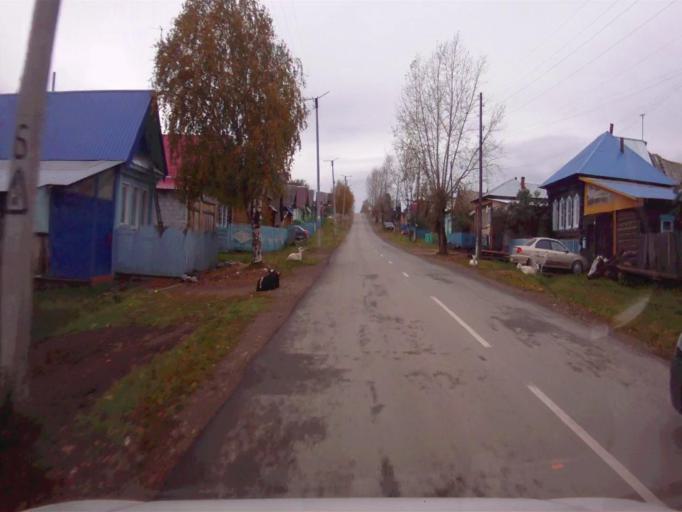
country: RU
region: Chelyabinsk
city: Nyazepetrovsk
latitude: 56.0588
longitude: 59.5836
